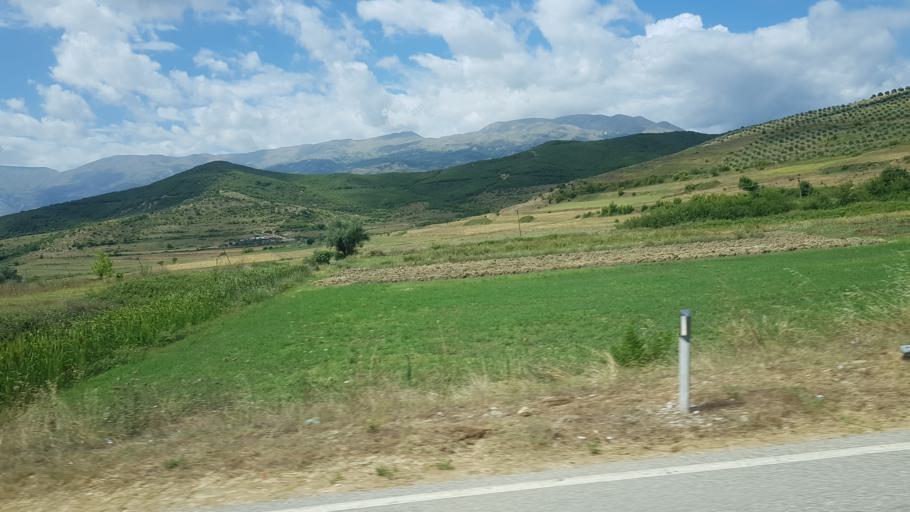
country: AL
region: Gjirokaster
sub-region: Rrethi i Tepelenes
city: Krahes
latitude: 40.4240
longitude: 19.8557
